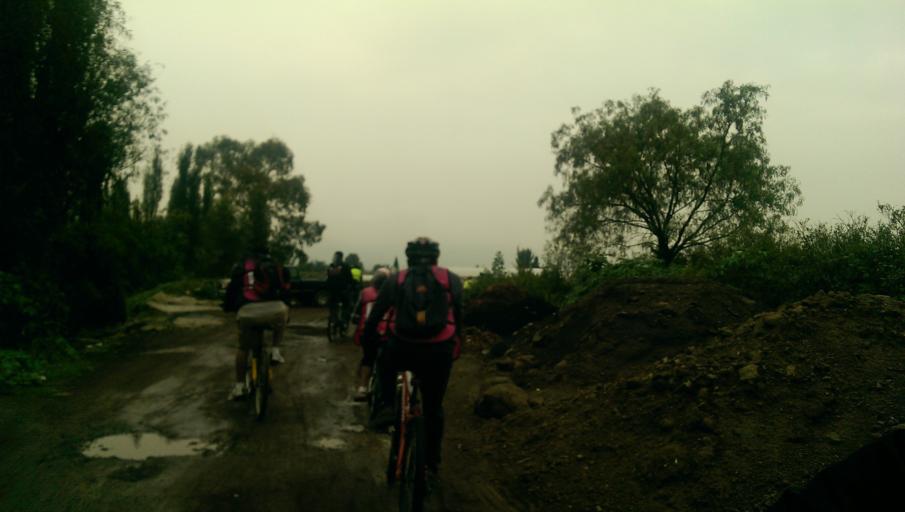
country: MX
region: Mexico City
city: Xochimilco
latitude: 19.2679
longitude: -99.0704
